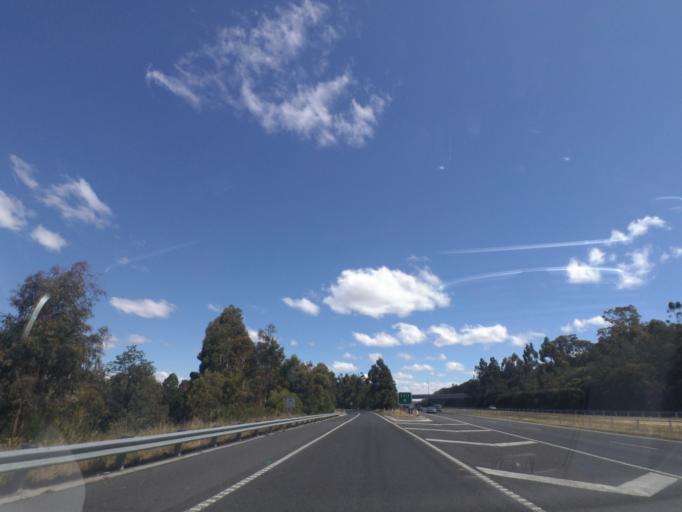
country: AU
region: Victoria
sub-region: Hume
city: Sunbury
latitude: -37.4120
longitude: 144.5452
